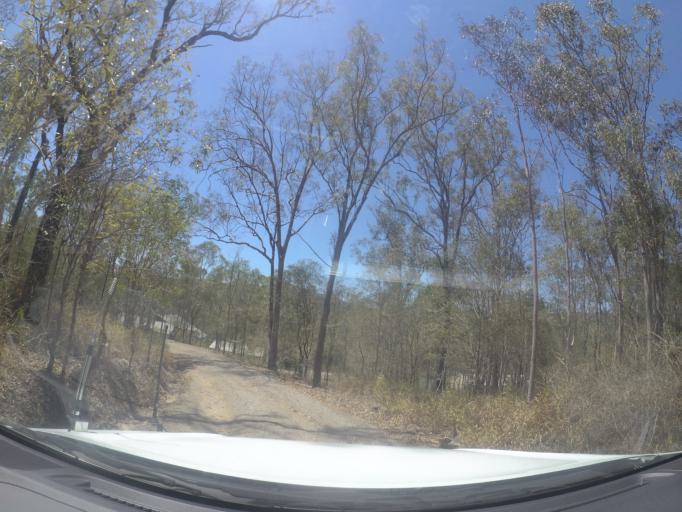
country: AU
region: Queensland
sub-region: Logan
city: Windaroo
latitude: -27.8061
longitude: 153.1681
